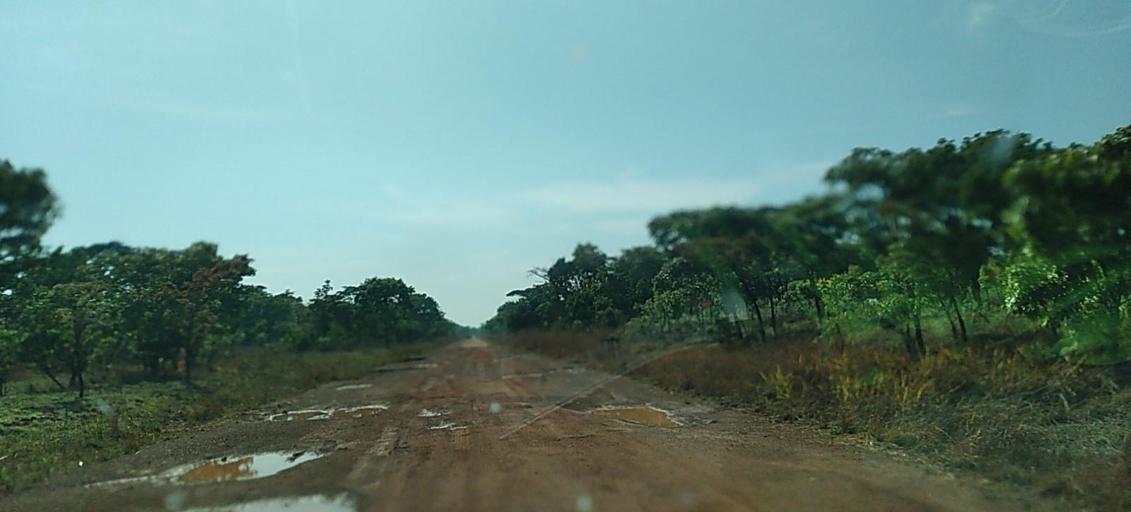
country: ZM
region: North-Western
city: Mwinilunga
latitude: -11.7893
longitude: 25.0592
